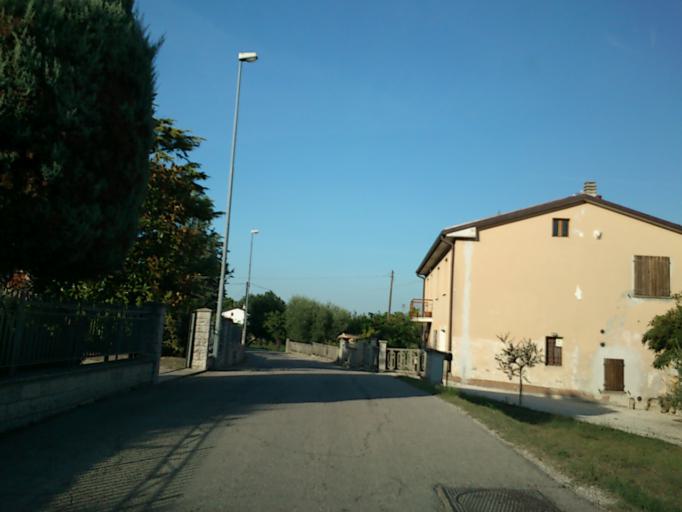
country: IT
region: The Marches
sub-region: Provincia di Pesaro e Urbino
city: Saltara
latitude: 43.7397
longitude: 12.9083
